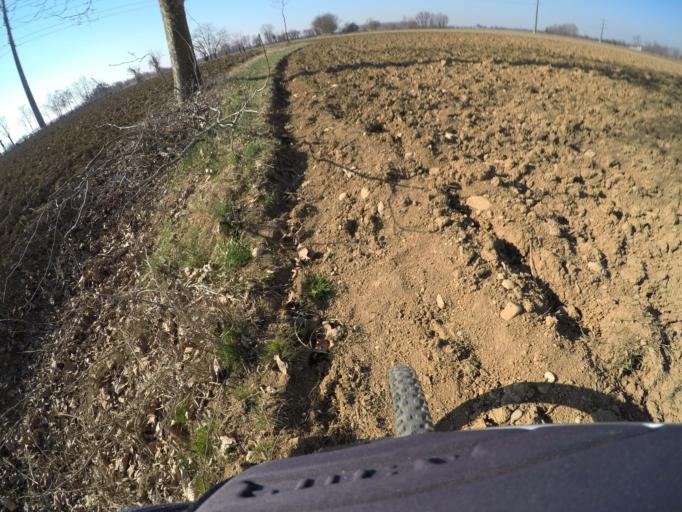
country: IT
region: Friuli Venezia Giulia
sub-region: Provincia di Udine
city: Lestizza
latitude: 45.9842
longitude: 13.1620
